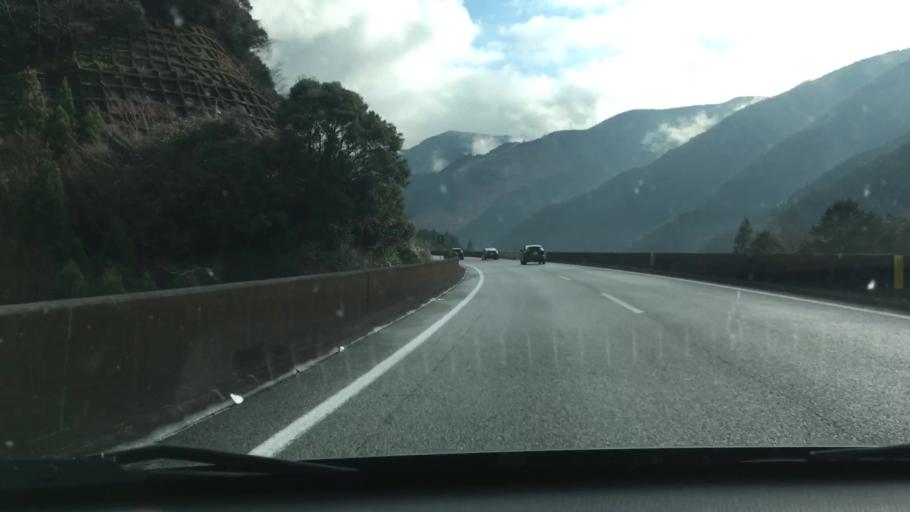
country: JP
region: Kumamoto
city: Yatsushiro
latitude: 32.4125
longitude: 130.6955
